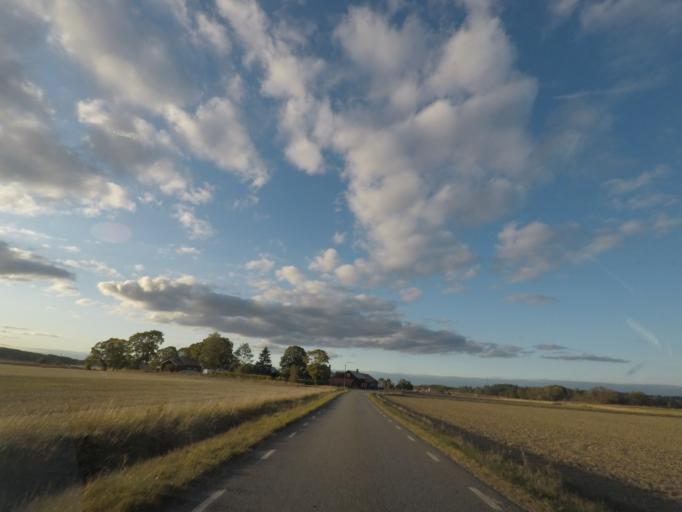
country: SE
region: Vaestmanland
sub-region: Kungsors Kommun
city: Kungsoer
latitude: 59.5255
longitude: 16.1146
